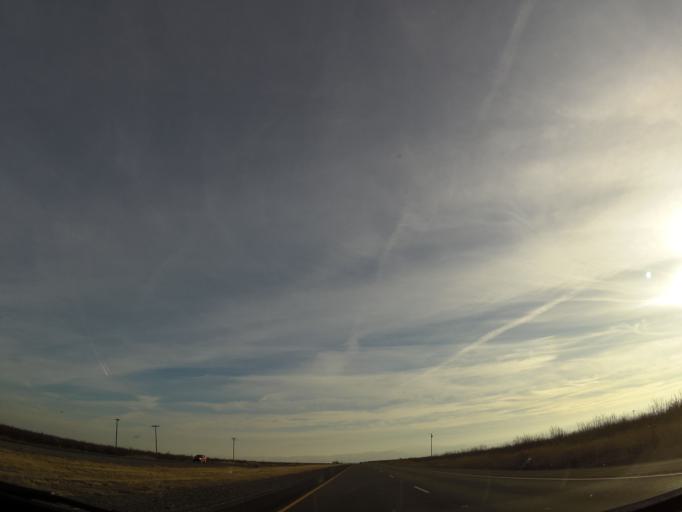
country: US
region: California
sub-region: San Joaquin County
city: Tracy
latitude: 37.7349
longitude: -121.3438
